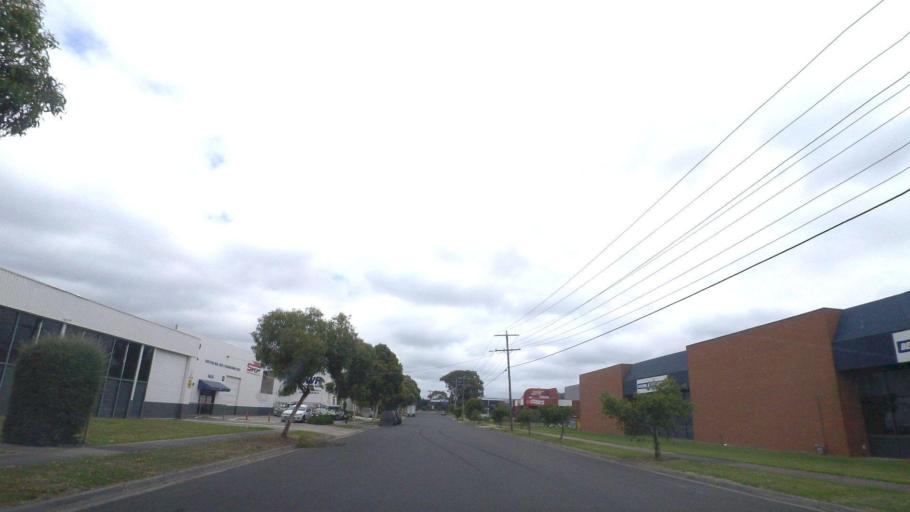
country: AU
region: Victoria
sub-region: Knox
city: Bayswater
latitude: -37.8478
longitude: 145.2798
